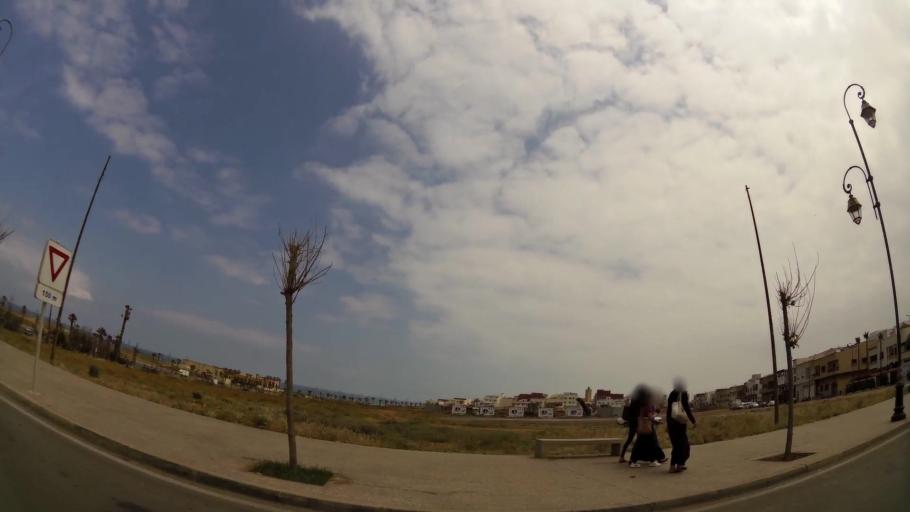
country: MA
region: Rabat-Sale-Zemmour-Zaer
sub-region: Skhirate-Temara
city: Temara
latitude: 33.9794
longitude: -6.8950
